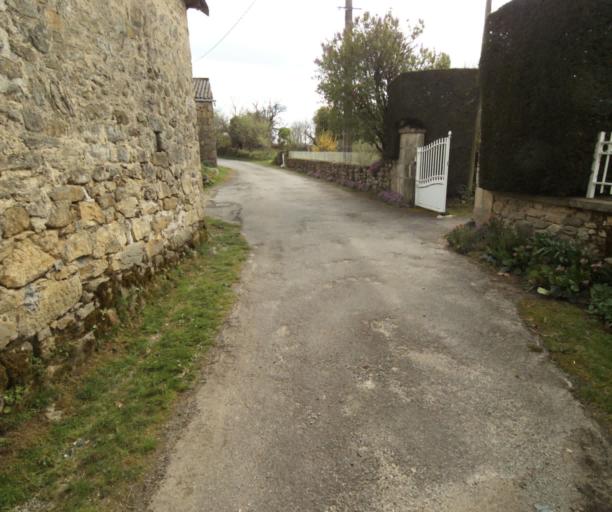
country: FR
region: Limousin
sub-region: Departement de la Correze
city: Argentat
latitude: 45.1830
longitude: 1.9344
